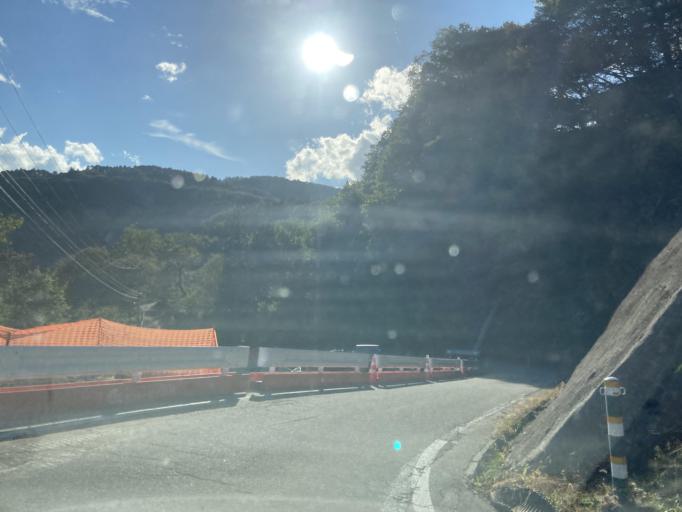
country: JP
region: Nagano
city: Omachi
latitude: 36.4883
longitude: 137.9124
